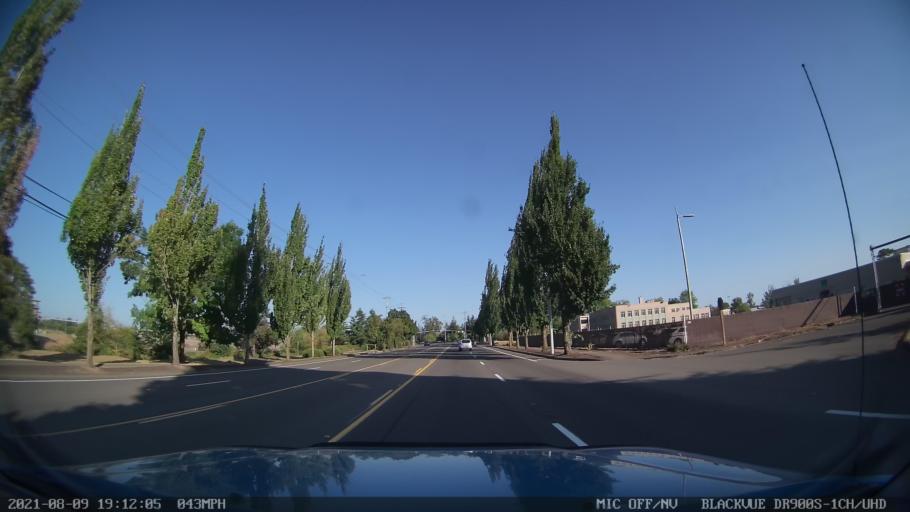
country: US
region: Oregon
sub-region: Marion County
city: Four Corners
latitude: 44.9304
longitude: -123.0058
